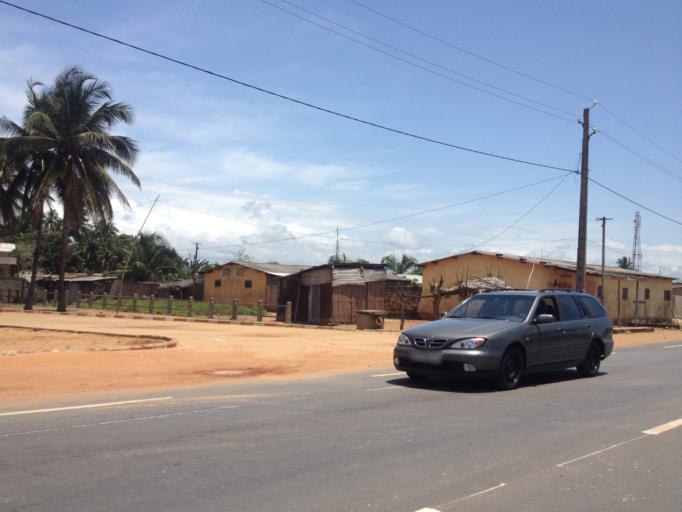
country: BJ
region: Mono
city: Grand-Popo
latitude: 6.2736
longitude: 1.7991
